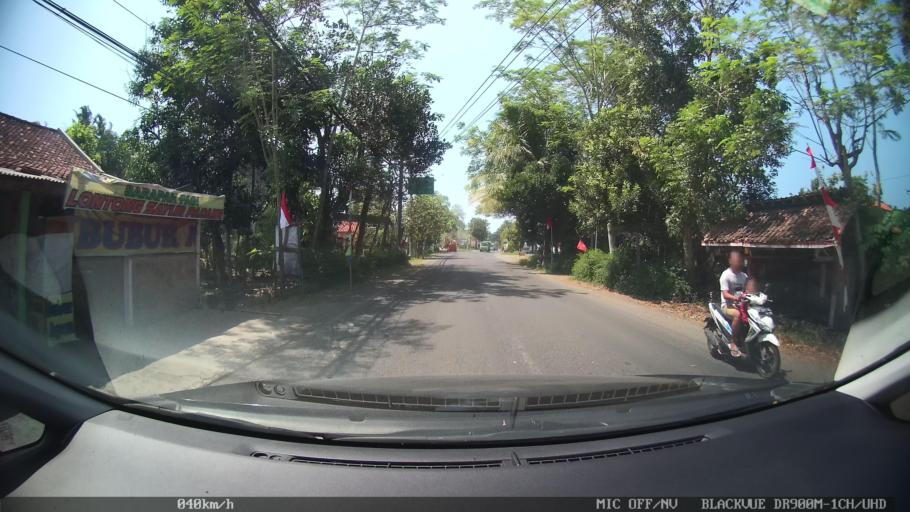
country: ID
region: Daerah Istimewa Yogyakarta
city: Srandakan
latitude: -7.9064
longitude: 110.0807
